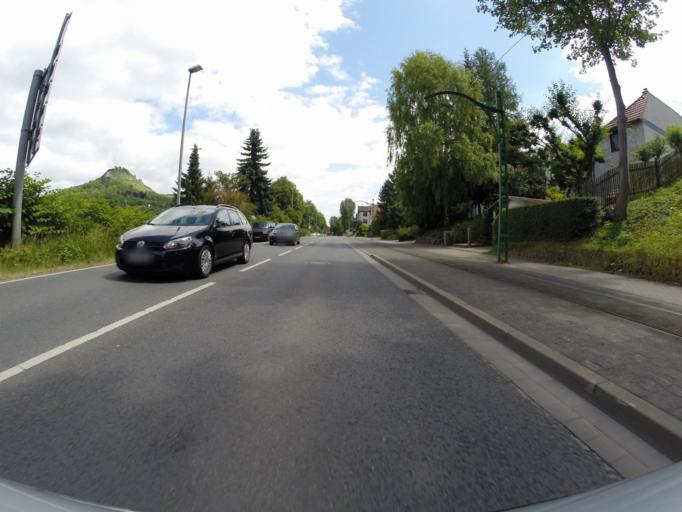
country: DE
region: Thuringia
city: Jena
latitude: 50.9342
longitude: 11.6084
